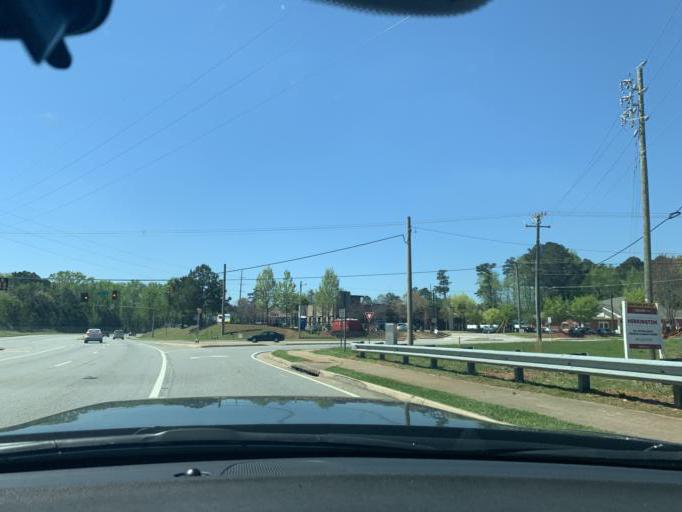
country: US
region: Georgia
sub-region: Forsyth County
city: Cumming
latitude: 34.1541
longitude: -84.1686
